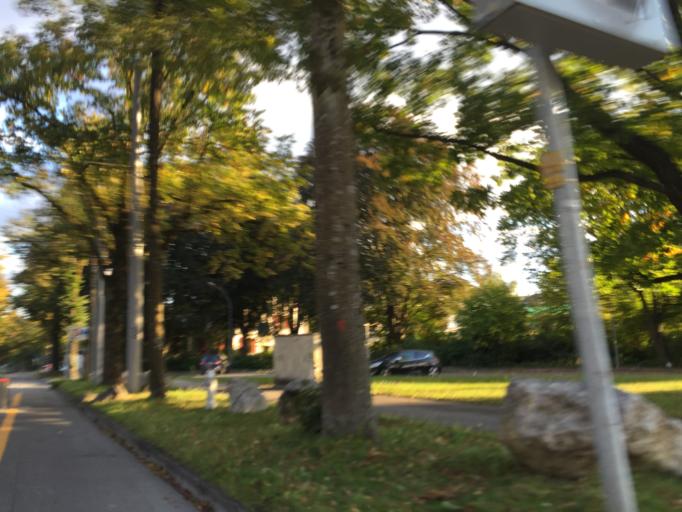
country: CH
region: Bern
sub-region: Bern-Mittelland District
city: Bern
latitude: 46.9611
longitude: 7.4337
